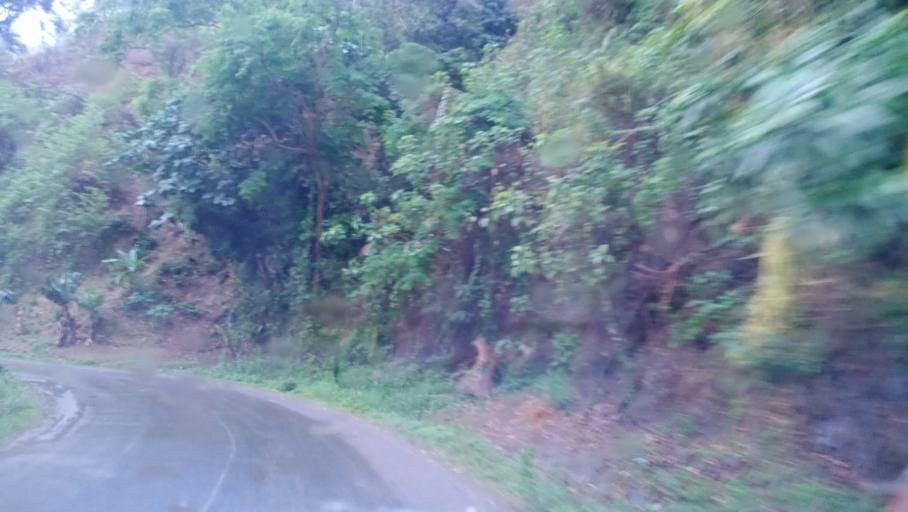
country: LA
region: Phongsali
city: Khoa
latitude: 21.0770
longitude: 102.5006
